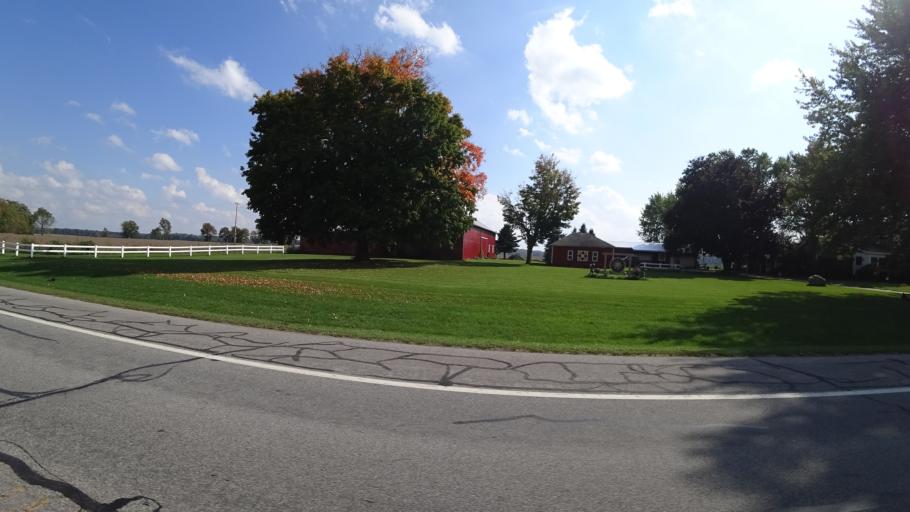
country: US
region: Michigan
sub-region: Saint Joseph County
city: Colon
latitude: 42.0284
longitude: -85.3455
